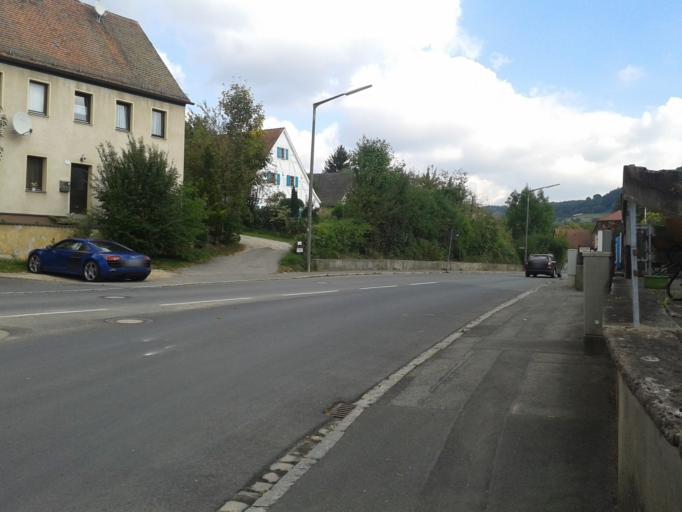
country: DE
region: Bavaria
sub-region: Regierungsbezirk Mittelfranken
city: Simmelsdorf
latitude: 49.5976
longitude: 11.3386
